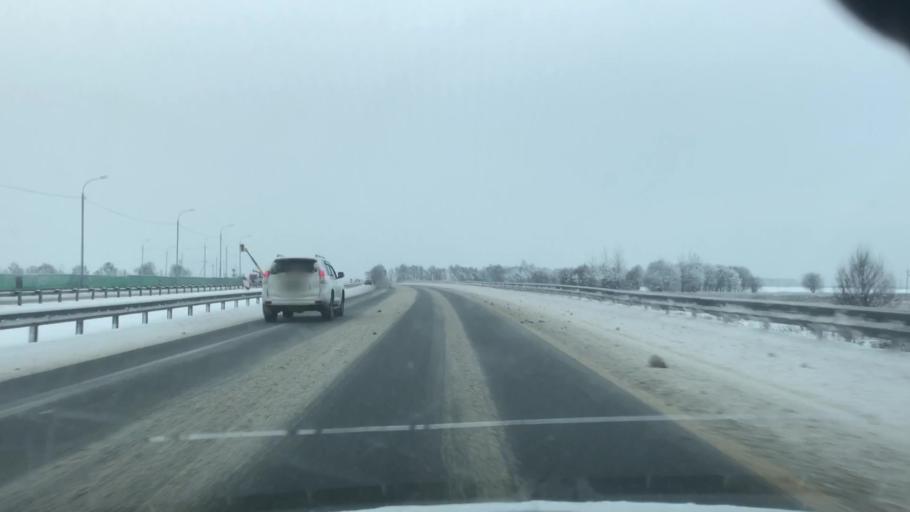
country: RU
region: Moskovskaya
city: Mikhnevo
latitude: 55.1167
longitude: 37.9269
